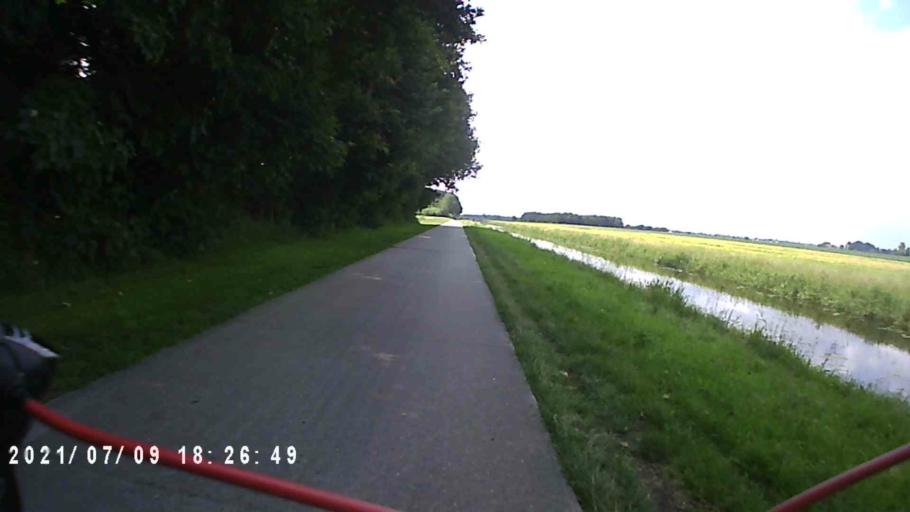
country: NL
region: Groningen
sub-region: Gemeente Pekela
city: Oude Pekela
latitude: 53.0547
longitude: 6.9853
